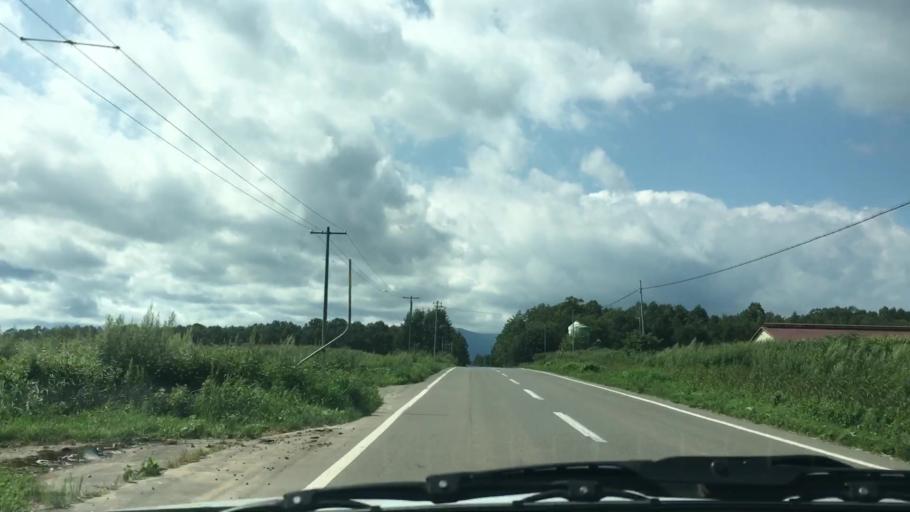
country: JP
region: Hokkaido
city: Otofuke
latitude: 43.2765
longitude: 143.3709
